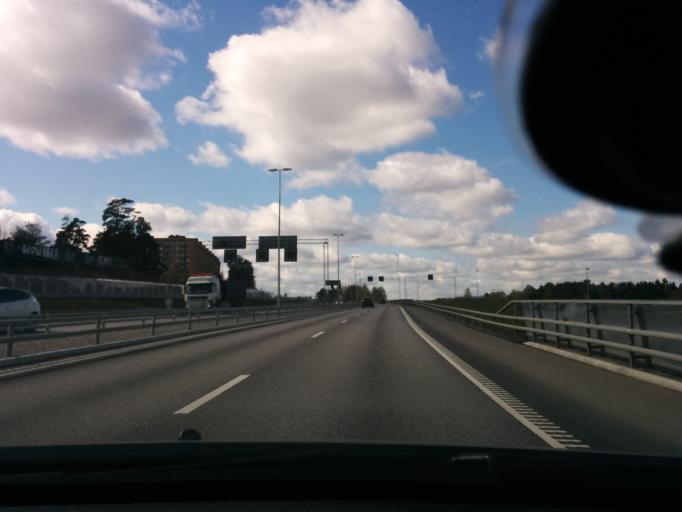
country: SE
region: Stockholm
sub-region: Stockholms Kommun
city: Kista
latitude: 59.3897
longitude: 17.9387
